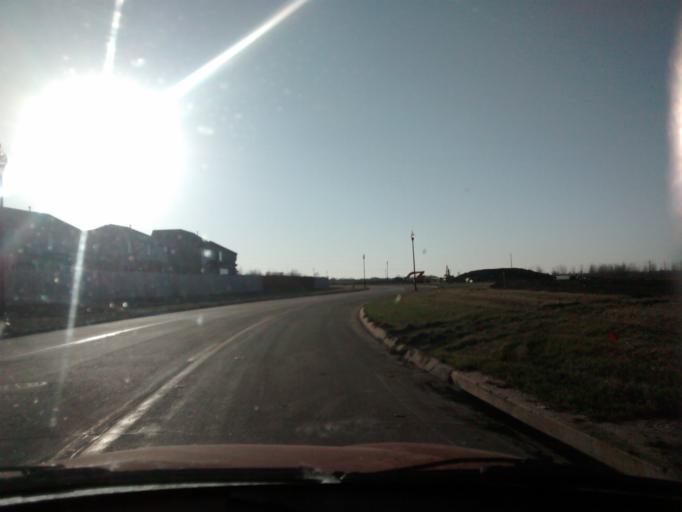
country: US
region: Nebraska
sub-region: Sarpy County
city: Papillion
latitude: 41.1454
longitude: -95.9802
